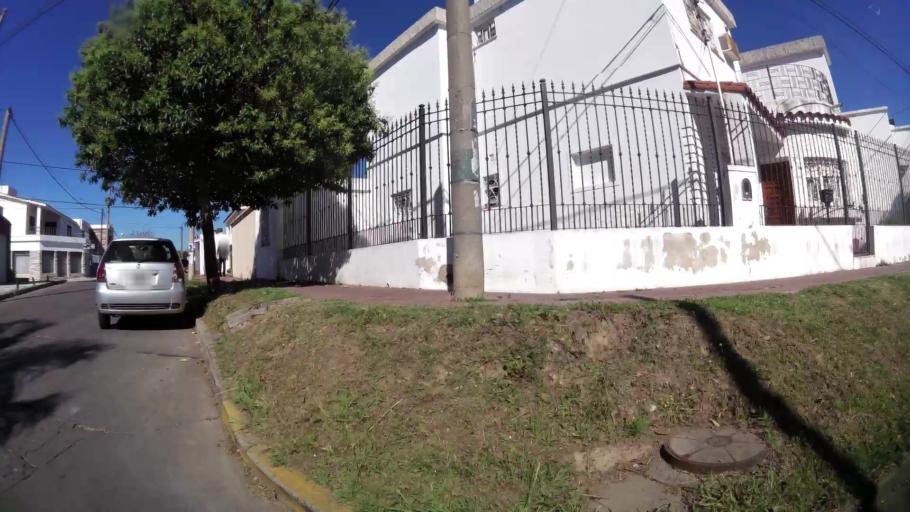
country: AR
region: Cordoba
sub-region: Departamento de Capital
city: Cordoba
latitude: -31.4336
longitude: -64.1572
